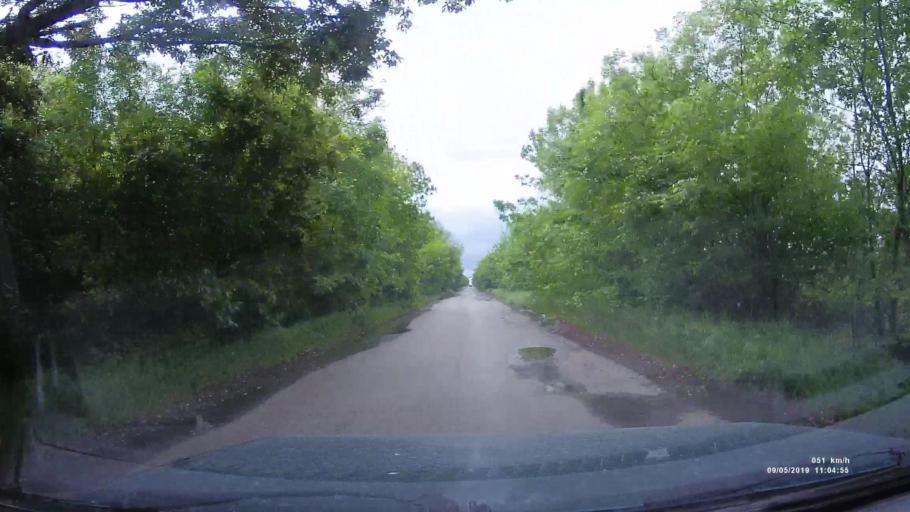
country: RU
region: Krasnodarskiy
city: Kanelovskaya
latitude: 46.8125
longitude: 39.2099
